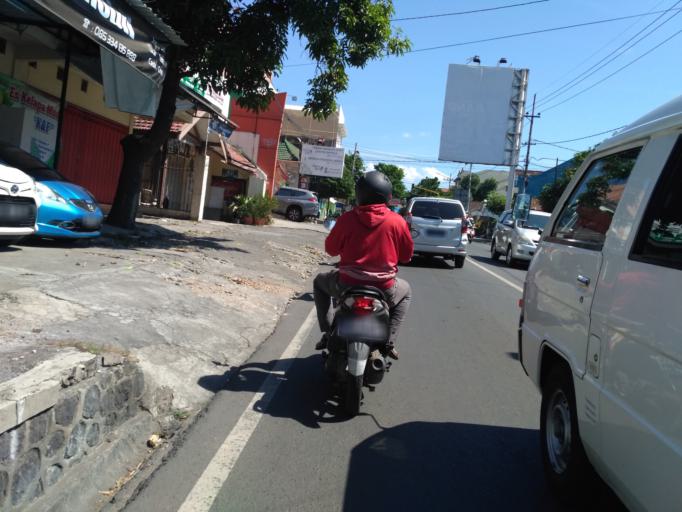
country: ID
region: East Java
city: Malang
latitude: -7.9793
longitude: 112.6502
